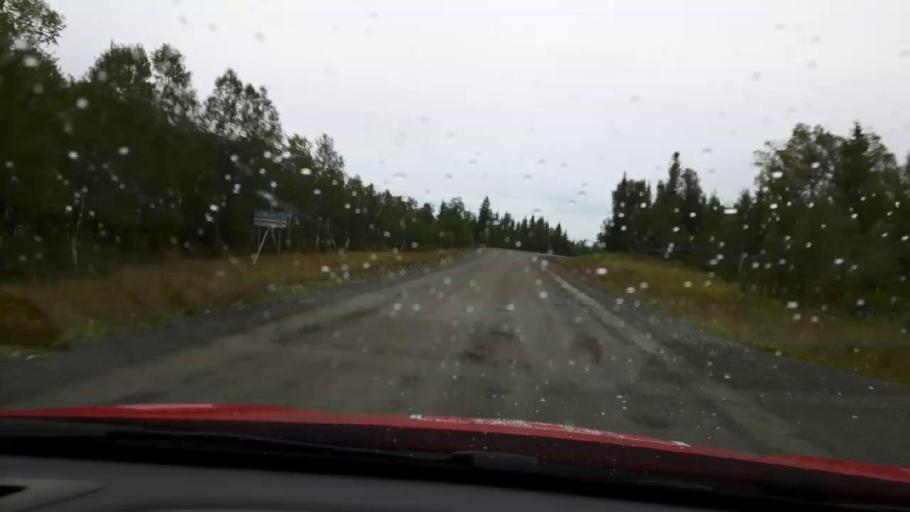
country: NO
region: Nord-Trondelag
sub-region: Meraker
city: Meraker
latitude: 63.5603
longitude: 12.2978
